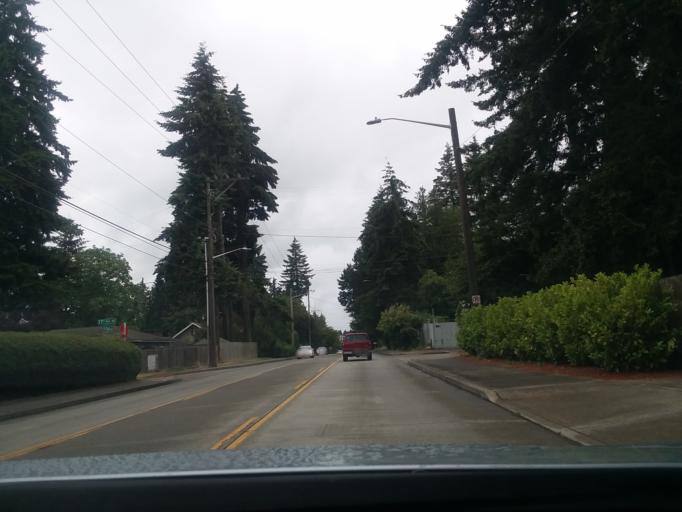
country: US
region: Washington
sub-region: King County
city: Lake Forest Park
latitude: 47.7085
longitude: -122.3096
